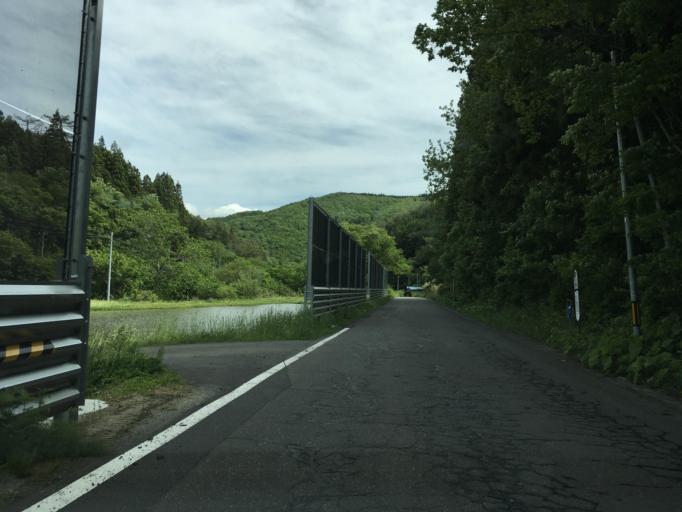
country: JP
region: Iwate
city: Mizusawa
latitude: 39.1021
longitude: 141.3342
